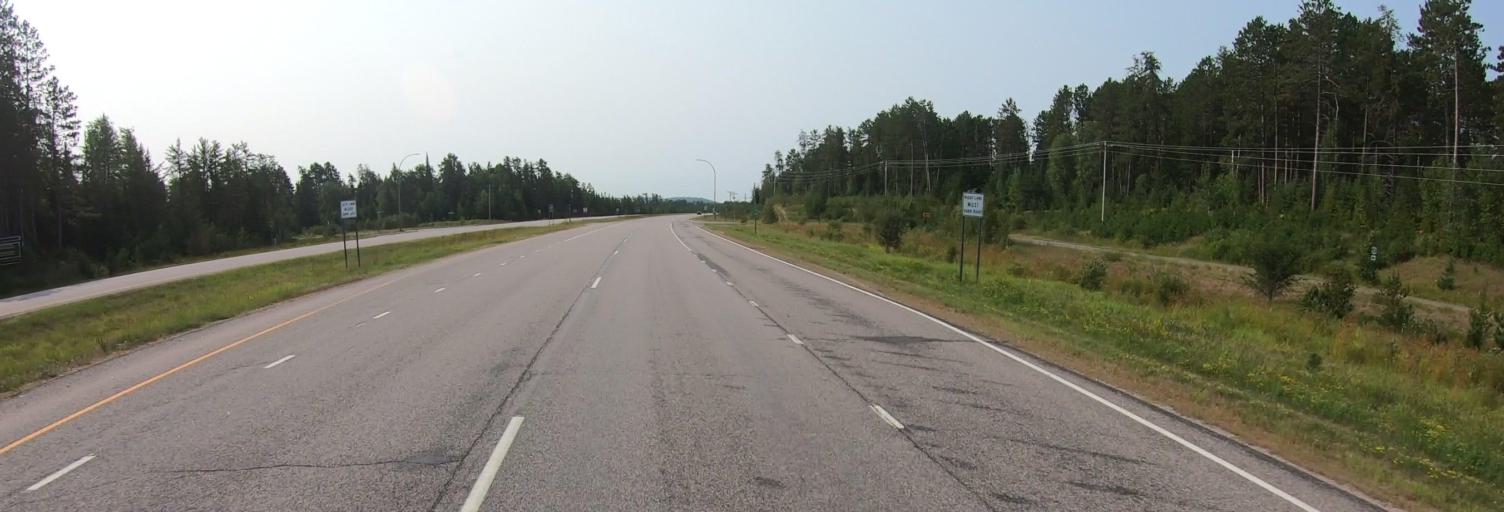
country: US
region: Minnesota
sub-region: Saint Louis County
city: Parkville
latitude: 47.6297
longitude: -92.5552
